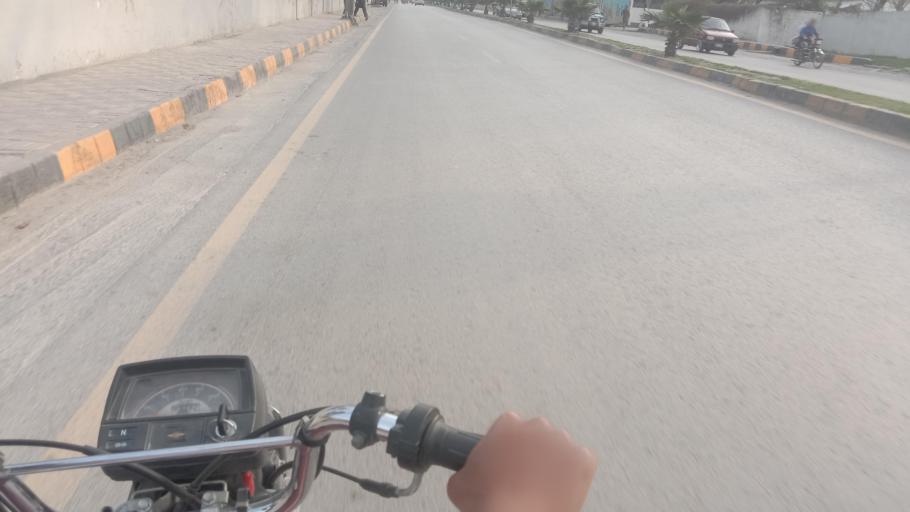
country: PK
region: Khyber Pakhtunkhwa
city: Abbottabad
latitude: 34.1642
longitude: 73.2229
